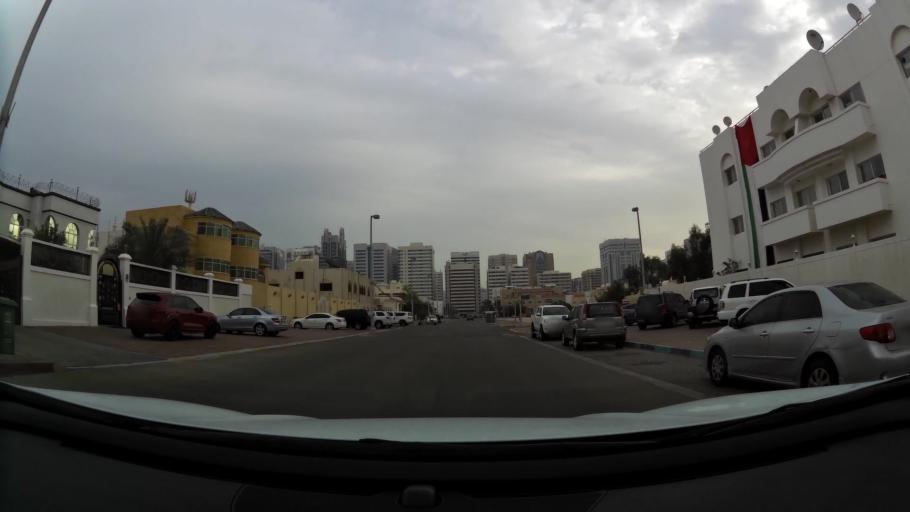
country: AE
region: Abu Dhabi
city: Abu Dhabi
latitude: 24.4833
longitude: 54.3695
